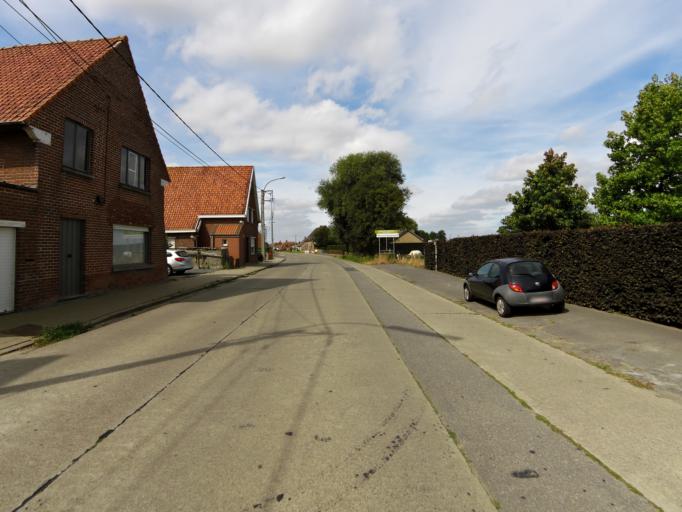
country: BE
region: Flanders
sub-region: Provincie West-Vlaanderen
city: Houthulst
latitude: 50.9386
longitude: 2.9343
